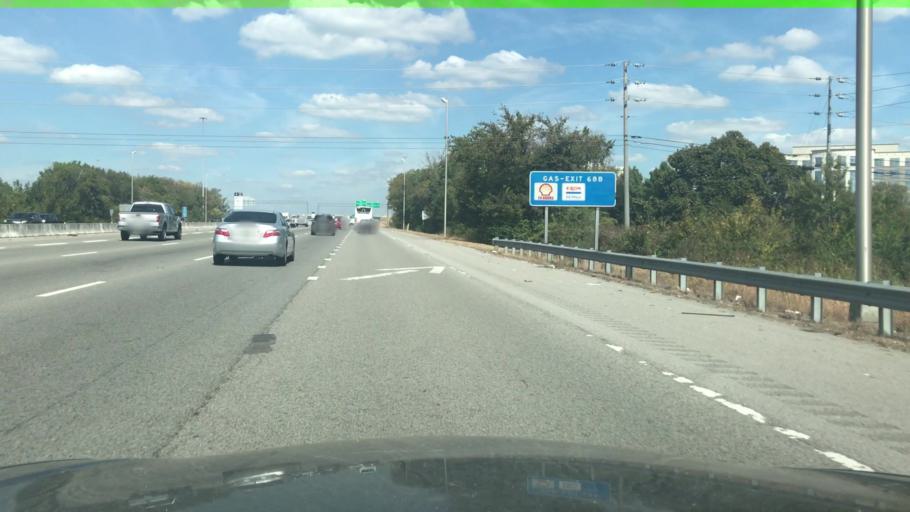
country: US
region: Tennessee
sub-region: Williamson County
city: Franklin
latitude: 35.9407
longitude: -86.8163
